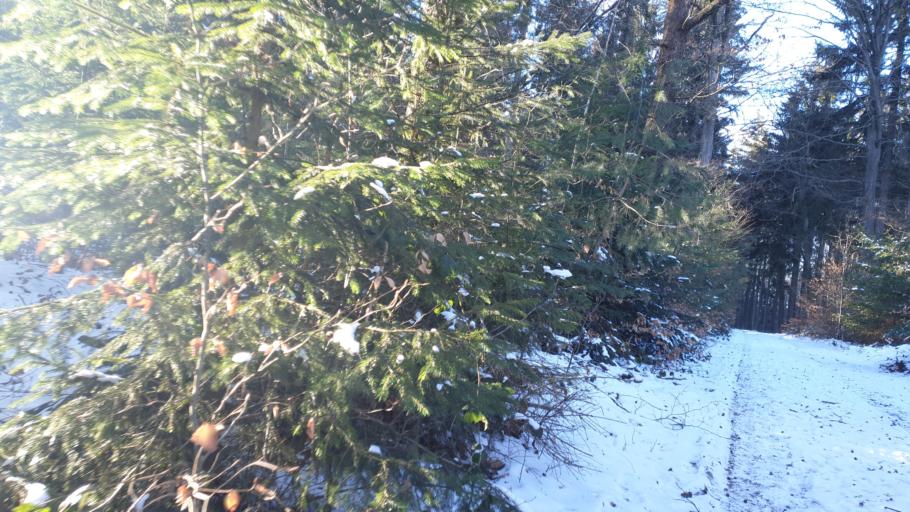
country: DE
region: Hesse
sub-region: Regierungsbezirk Darmstadt
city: Beerfelden
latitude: 49.5461
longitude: 8.9989
